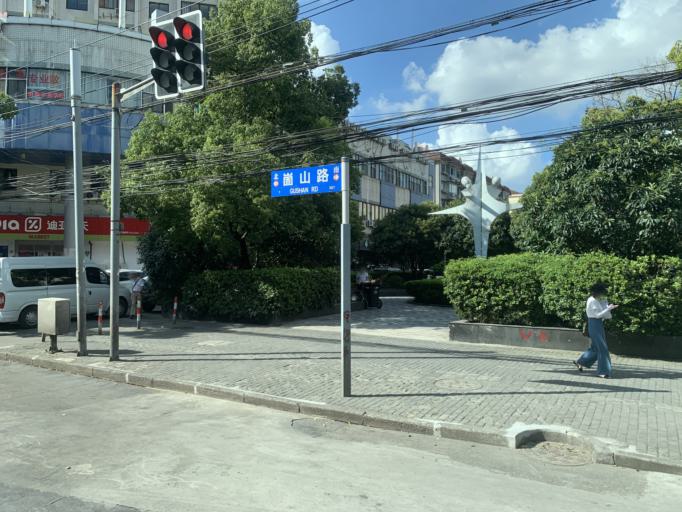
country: CN
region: Shanghai Shi
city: Pudong
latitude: 31.2491
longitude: 121.5468
